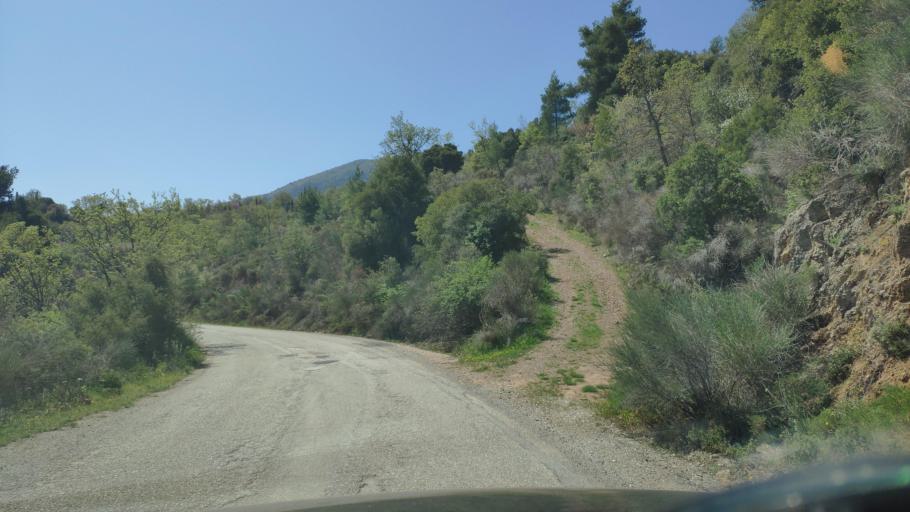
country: GR
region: West Greece
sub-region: Nomos Achaias
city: Akrata
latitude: 38.0885
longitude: 22.3233
